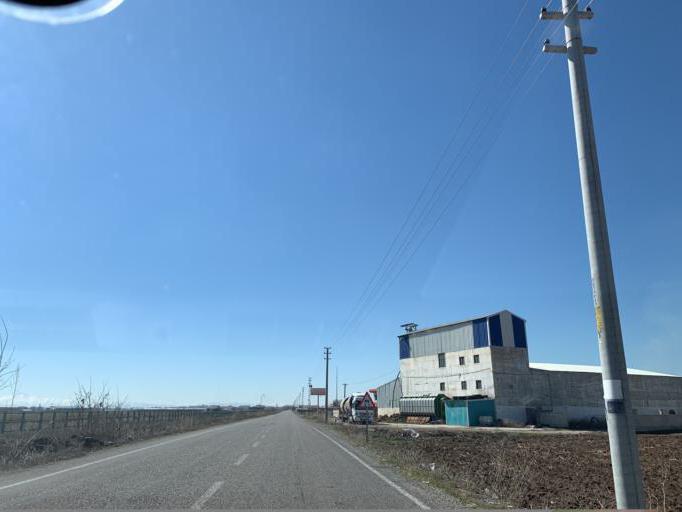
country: TR
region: Konya
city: Cumra
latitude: 37.5979
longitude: 32.7907
